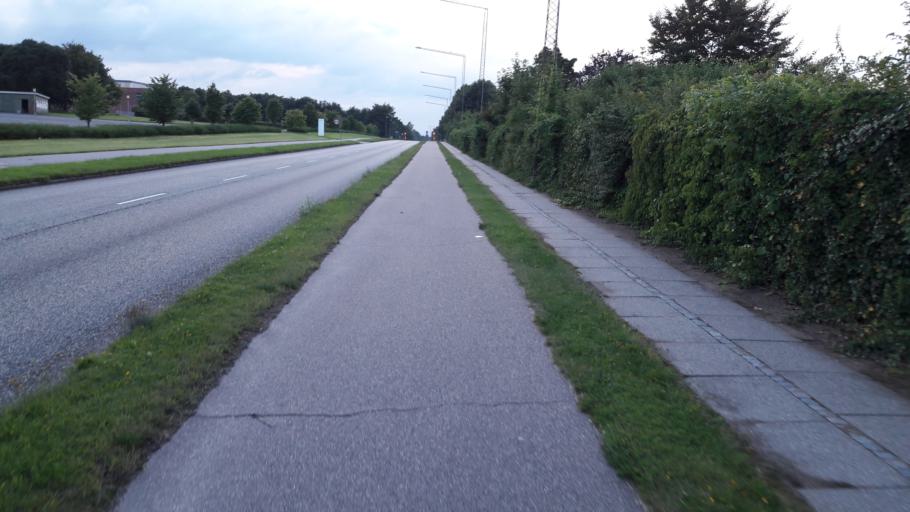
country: DK
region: Central Jutland
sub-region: Arhus Kommune
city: Arhus
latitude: 56.1968
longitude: 10.2072
